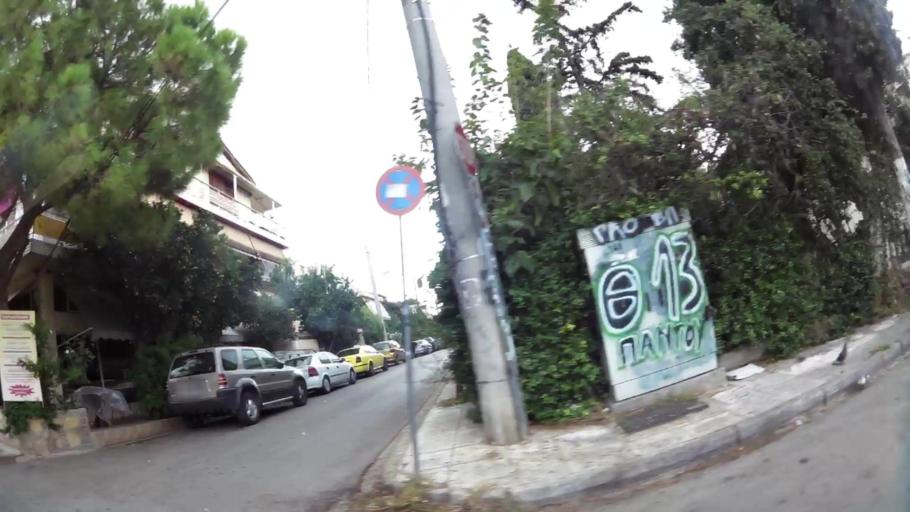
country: GR
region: Attica
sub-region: Nomarchia Athinas
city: Melissia
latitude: 38.0561
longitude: 23.8238
